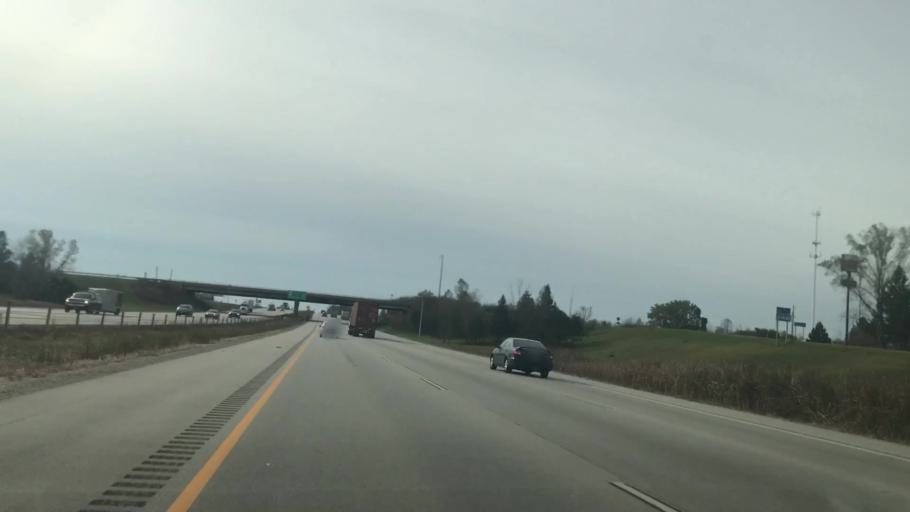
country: US
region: Wisconsin
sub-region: Washington County
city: Richfield
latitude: 43.2531
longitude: -88.1819
